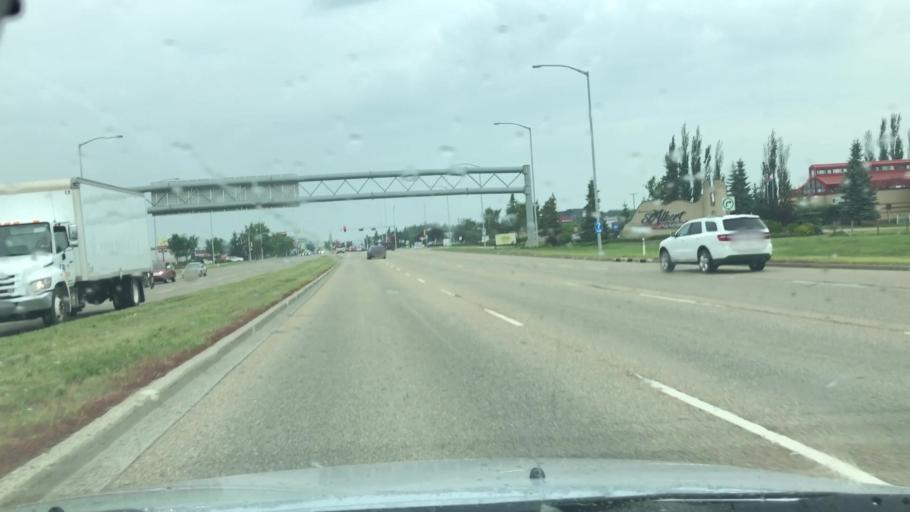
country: CA
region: Alberta
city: St. Albert
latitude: 53.6187
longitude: -113.6037
